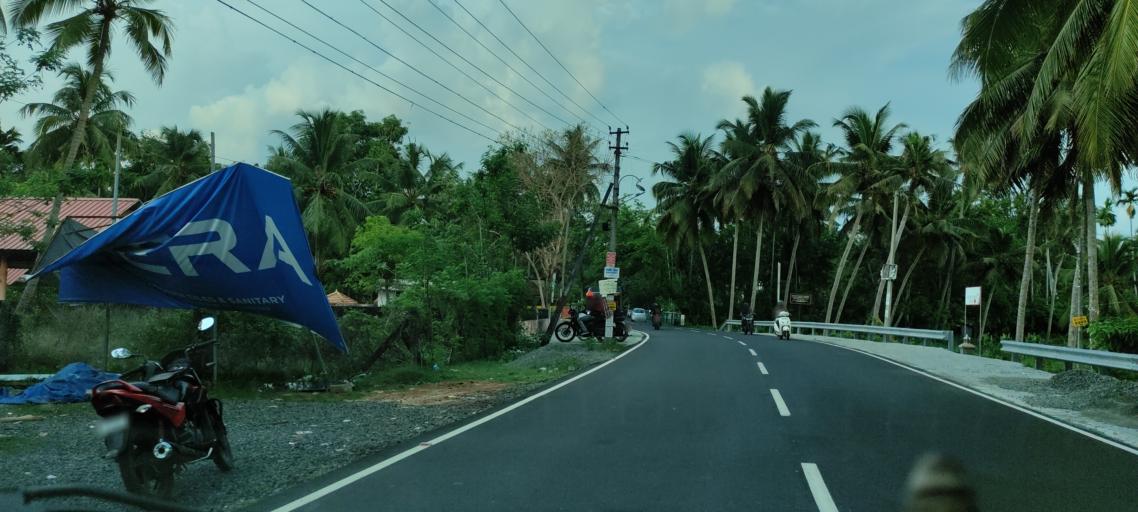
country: IN
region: Kerala
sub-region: Alappuzha
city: Kutiatodu
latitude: 9.8227
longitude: 76.3448
